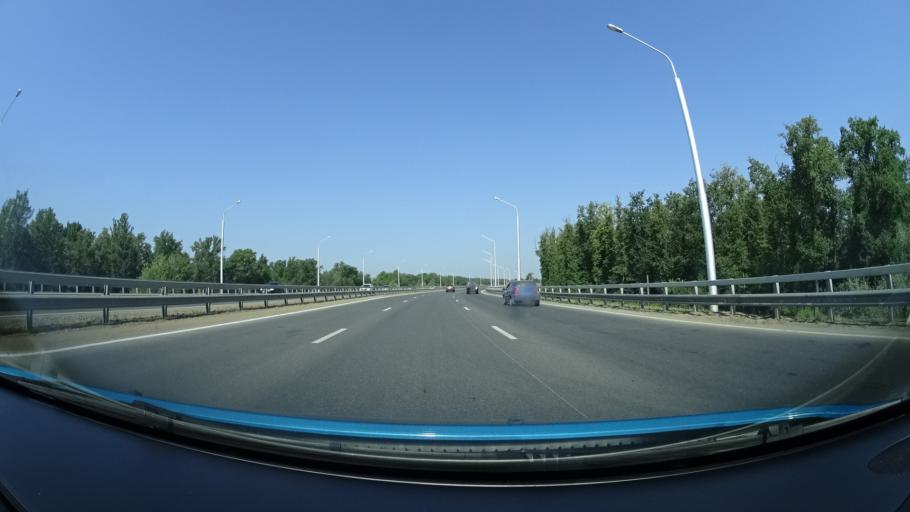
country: RU
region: Bashkortostan
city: Mikhaylovka
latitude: 54.7808
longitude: 55.9172
